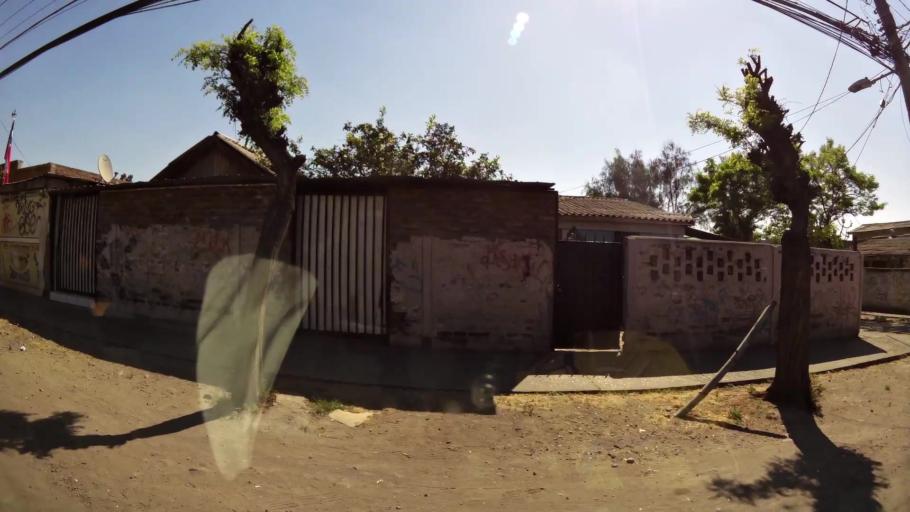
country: CL
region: Santiago Metropolitan
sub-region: Provincia de Maipo
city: San Bernardo
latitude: -33.5827
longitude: -70.7053
